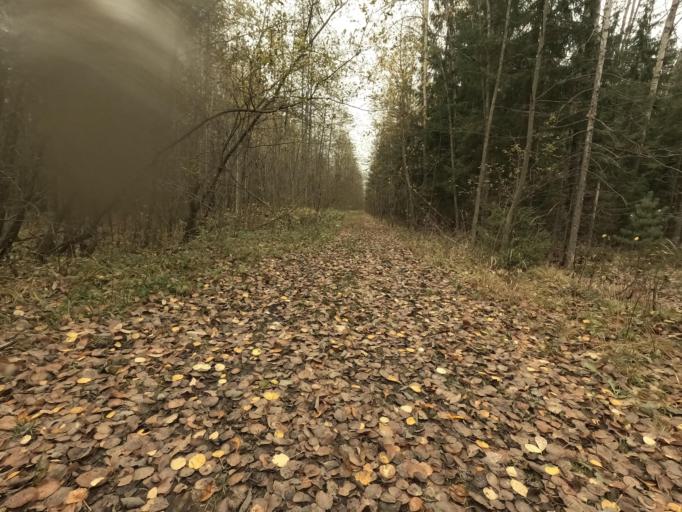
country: RU
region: Leningrad
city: Pavlovo
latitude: 59.7703
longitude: 30.9139
